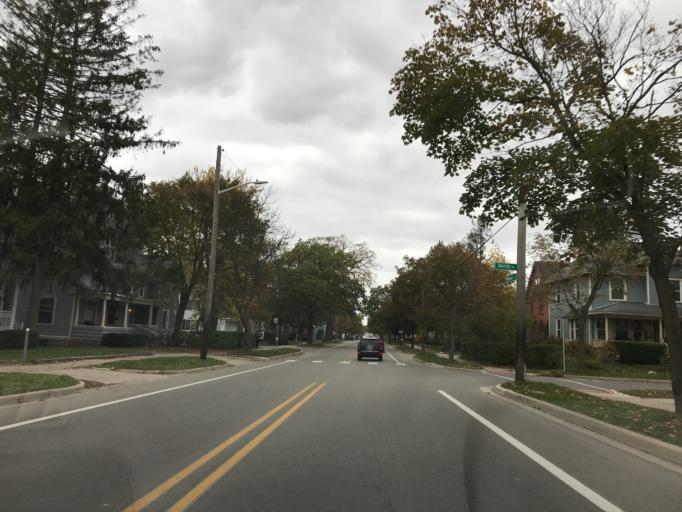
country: US
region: Michigan
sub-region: Washtenaw County
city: Ann Arbor
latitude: 42.2674
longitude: -83.7369
